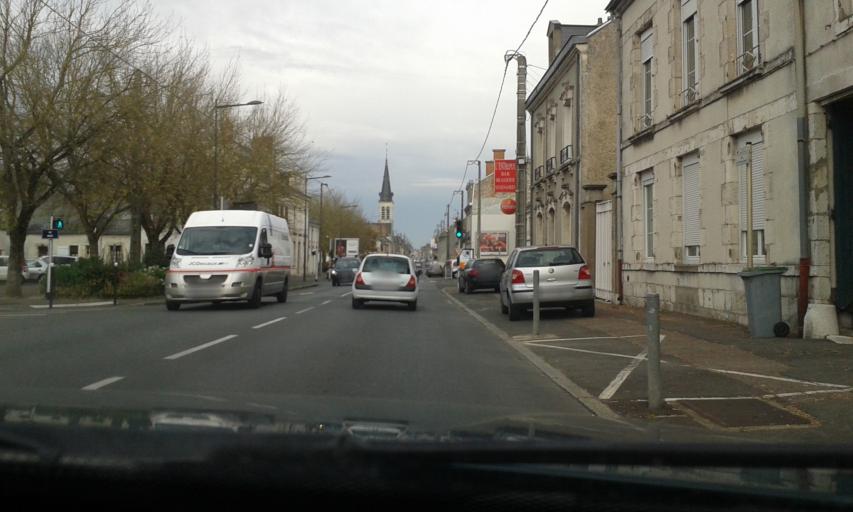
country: FR
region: Centre
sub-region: Departement du Loiret
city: Fleury-les-Aubrais
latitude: 47.9266
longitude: 1.8965
